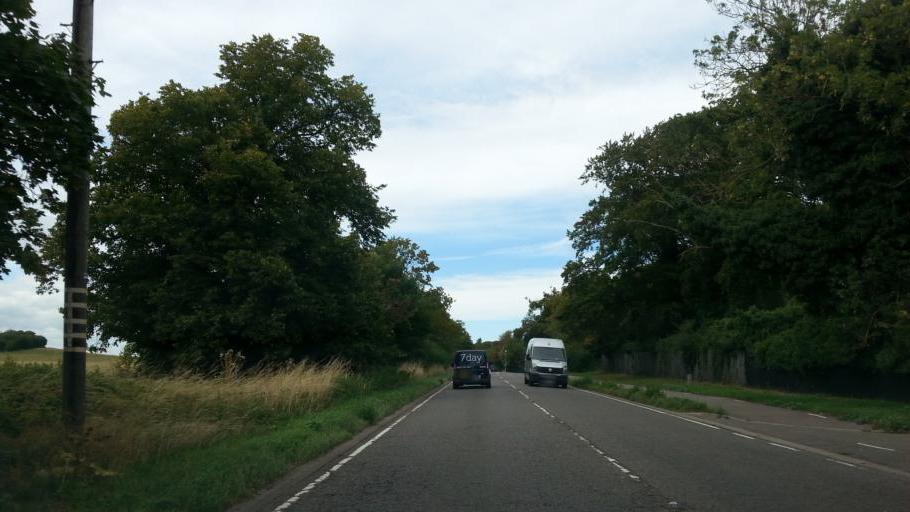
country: GB
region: England
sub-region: Cambridgeshire
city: Sawston
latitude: 52.1524
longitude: 0.1880
